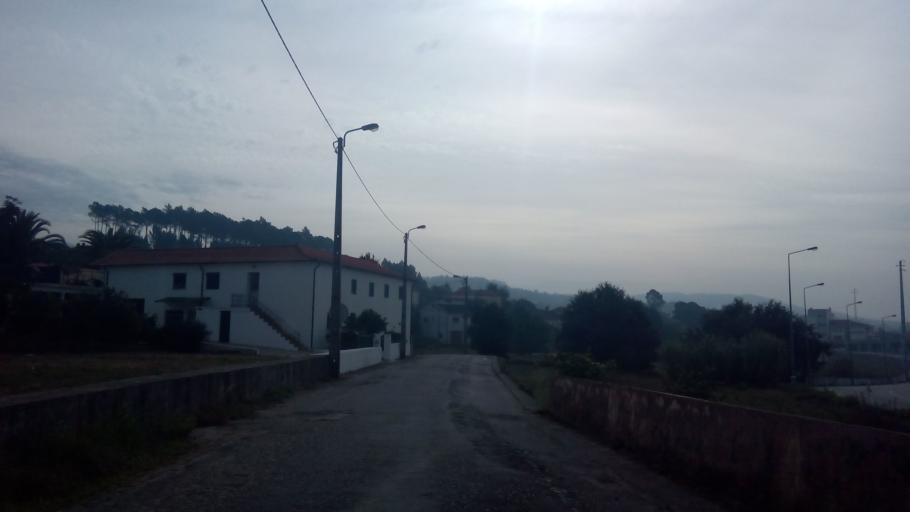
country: PT
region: Porto
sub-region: Paredes
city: Gandra
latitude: 41.1985
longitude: -8.4357
